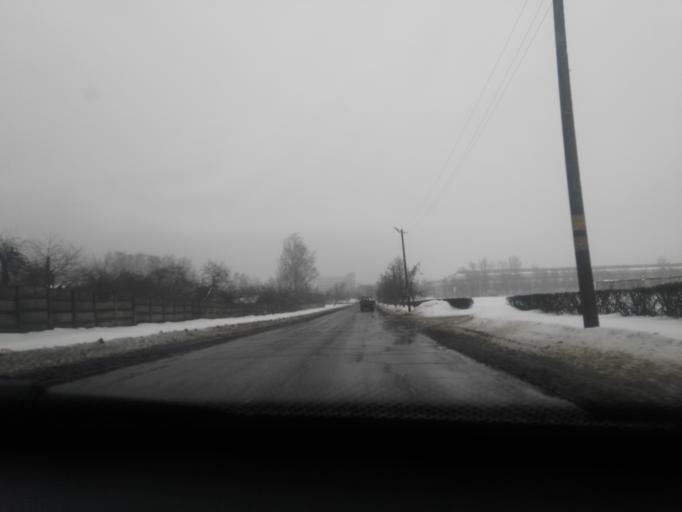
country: BY
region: Mogilev
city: Babruysk
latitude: 53.1864
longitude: 29.2129
